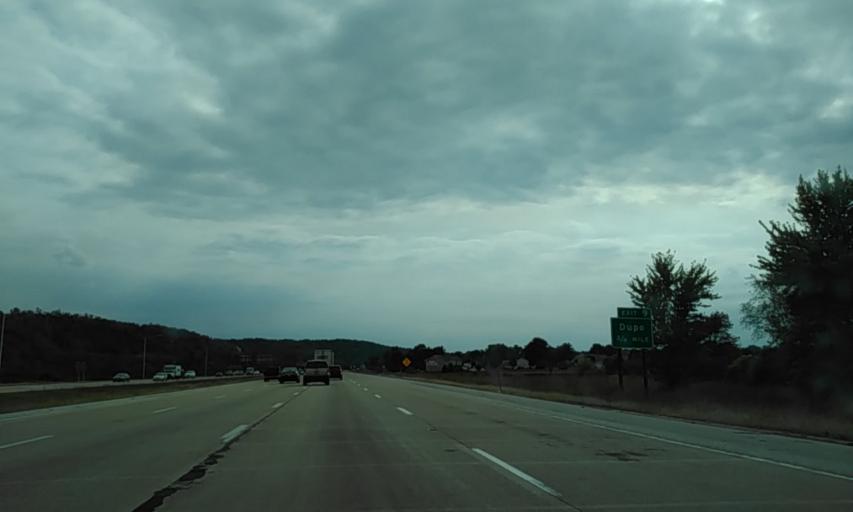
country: US
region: Illinois
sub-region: Saint Clair County
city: Dupo
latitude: 38.5226
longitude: -90.1994
